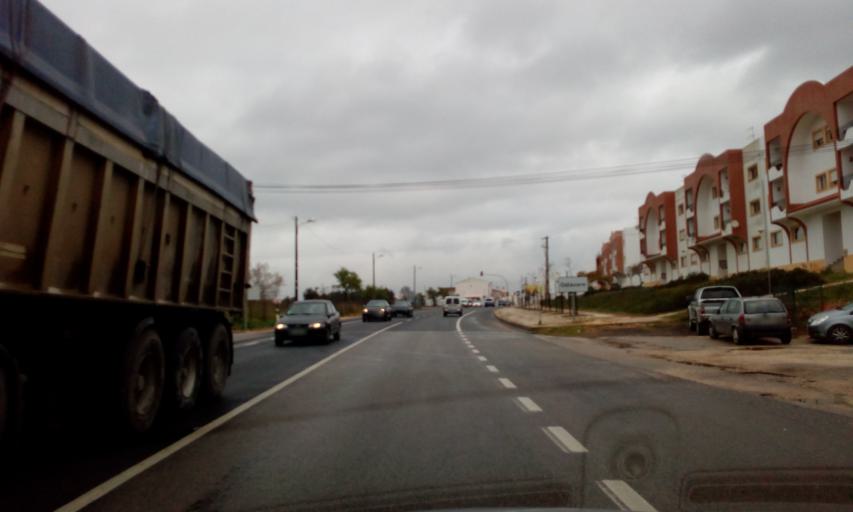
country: PT
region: Faro
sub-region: Lagos
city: Lagos
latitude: 37.1455
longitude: -8.6609
